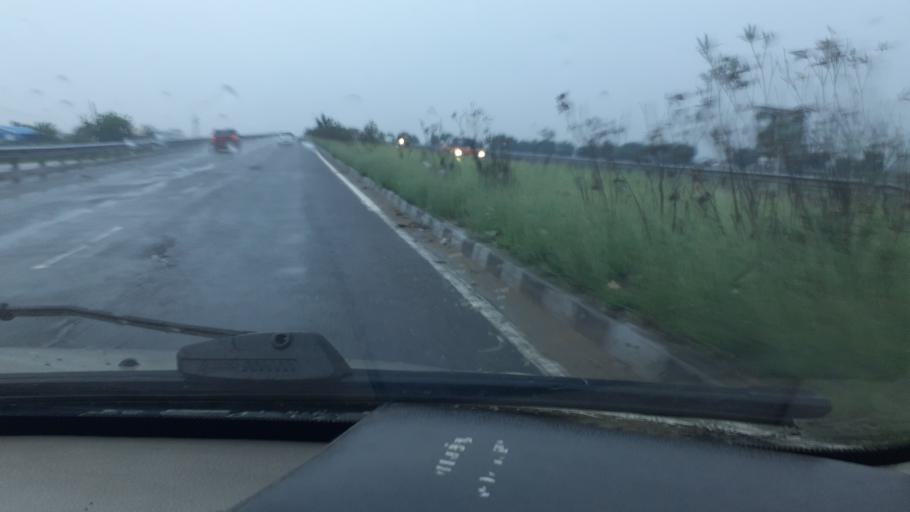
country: IN
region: Tamil Nadu
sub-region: Virudhunagar
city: Sattur
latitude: 9.3835
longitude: 77.9141
